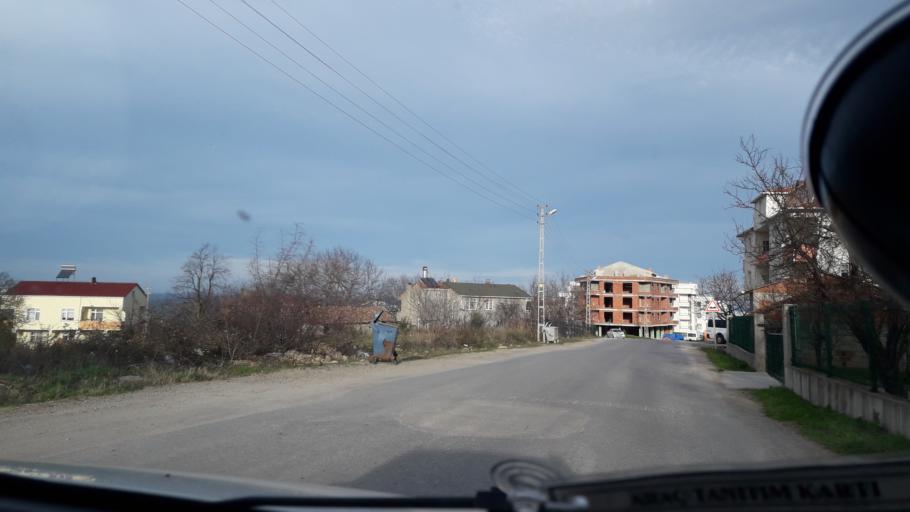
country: TR
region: Sinop
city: Gerze
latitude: 41.8032
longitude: 35.1816
